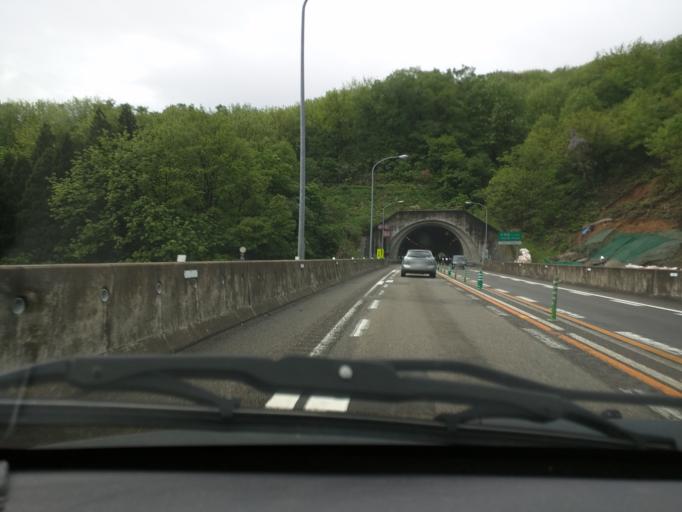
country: JP
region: Niigata
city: Arai
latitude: 37.0491
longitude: 138.2326
